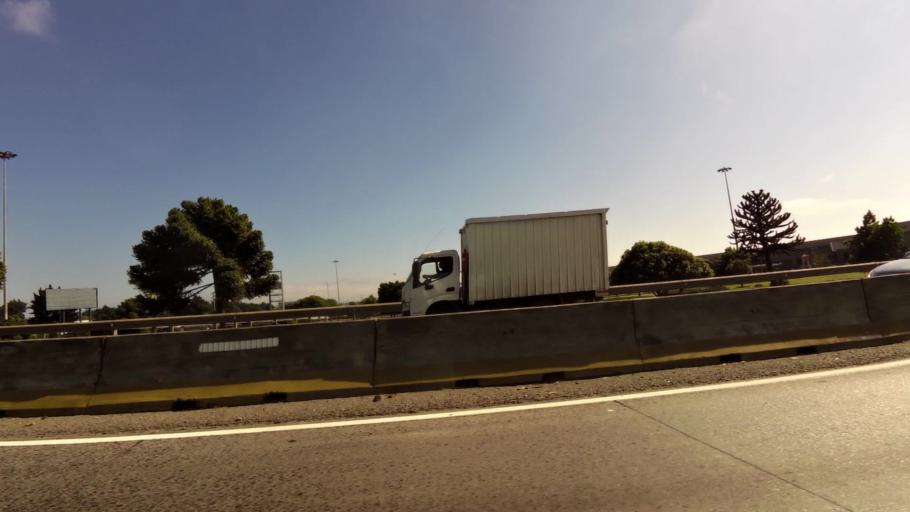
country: CL
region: Biobio
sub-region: Provincia de Concepcion
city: Concepcion
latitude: -36.7950
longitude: -73.0674
